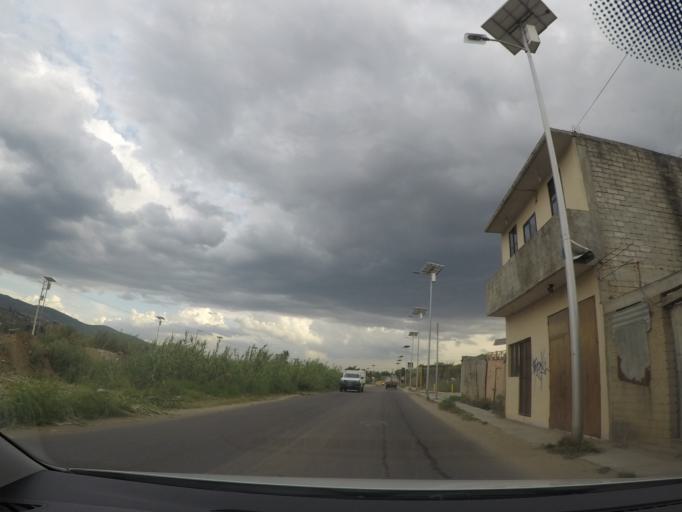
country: MX
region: Oaxaca
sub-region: San Antonio de la Cal
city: San Antonio de la Cal
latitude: 17.0503
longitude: -96.7051
